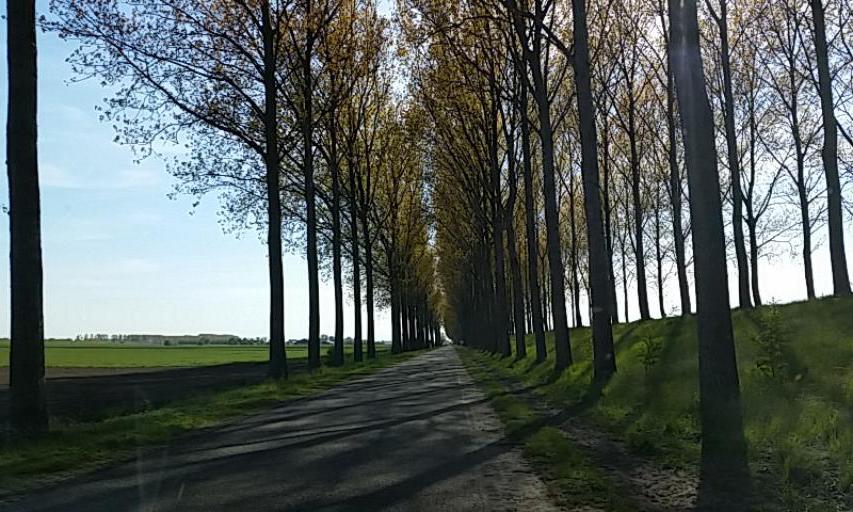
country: NL
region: Zeeland
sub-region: Gemeente Borsele
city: Borssele
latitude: 51.3411
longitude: 3.7301
